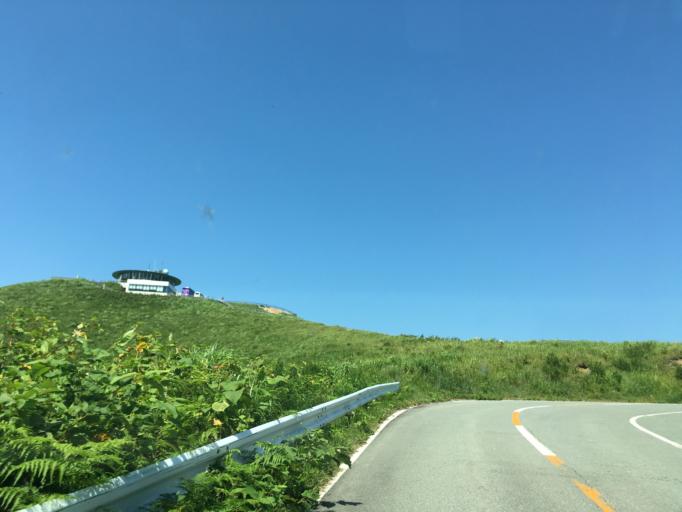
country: JP
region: Akita
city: Tenno
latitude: 39.9315
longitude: 139.8751
